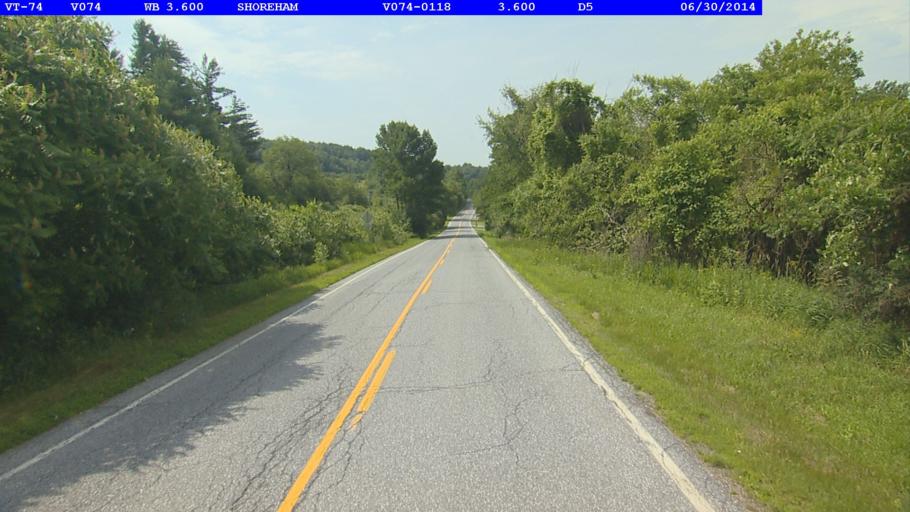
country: US
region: New York
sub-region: Essex County
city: Ticonderoga
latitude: 43.8837
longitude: -73.3335
